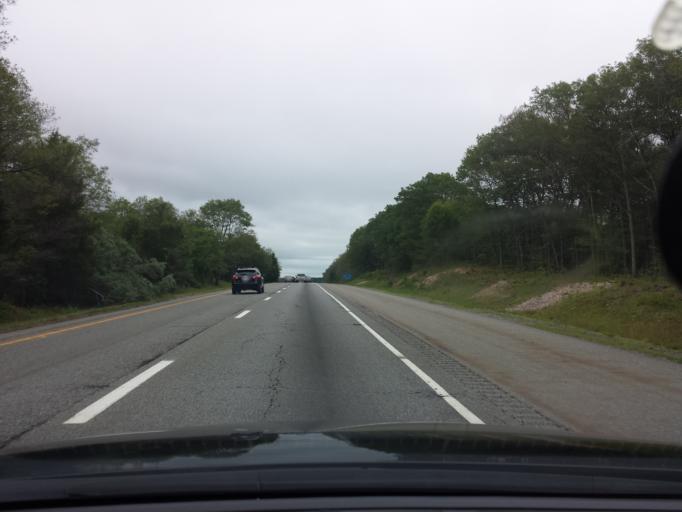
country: US
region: Connecticut
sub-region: New London County
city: Pawcatuck
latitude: 41.4032
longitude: -71.8617
